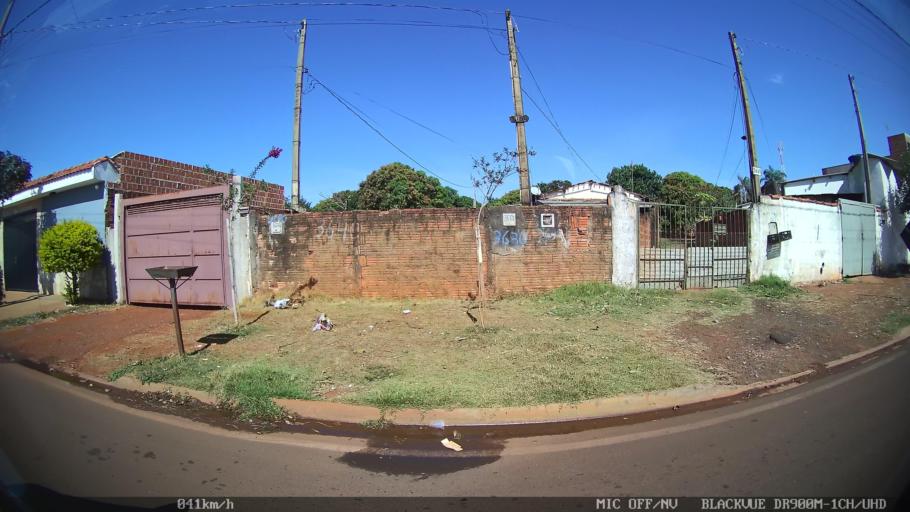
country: BR
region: Sao Paulo
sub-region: Batatais
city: Batatais
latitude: -20.8835
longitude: -47.5680
